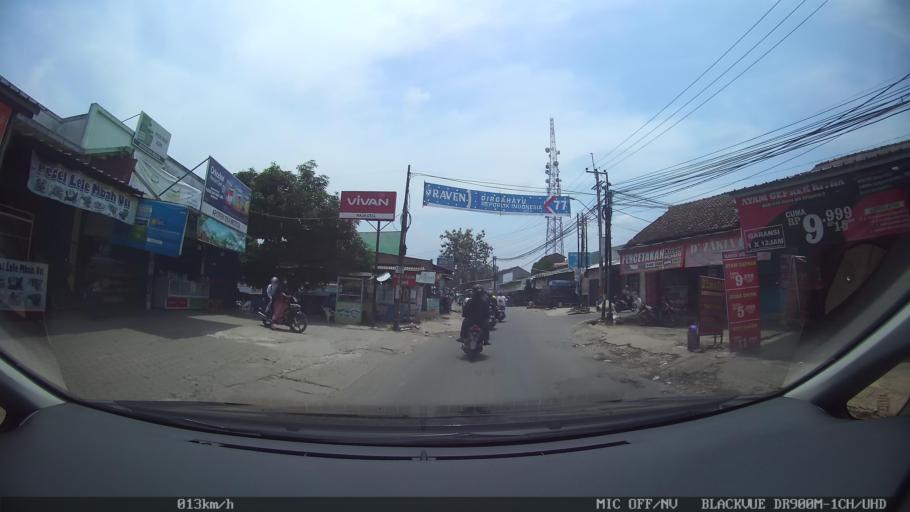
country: ID
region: Lampung
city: Kedaton
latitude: -5.3543
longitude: 105.2386
